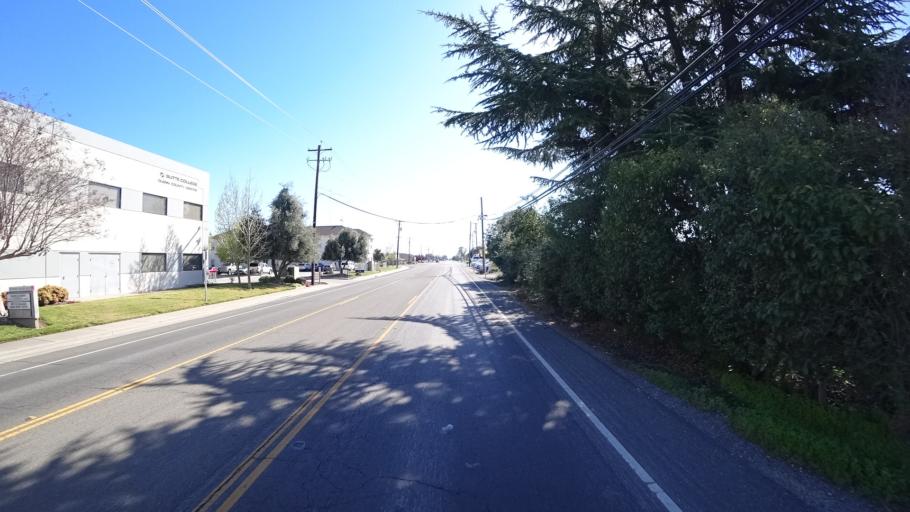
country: US
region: California
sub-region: Glenn County
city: Orland
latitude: 39.7472
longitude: -122.1748
